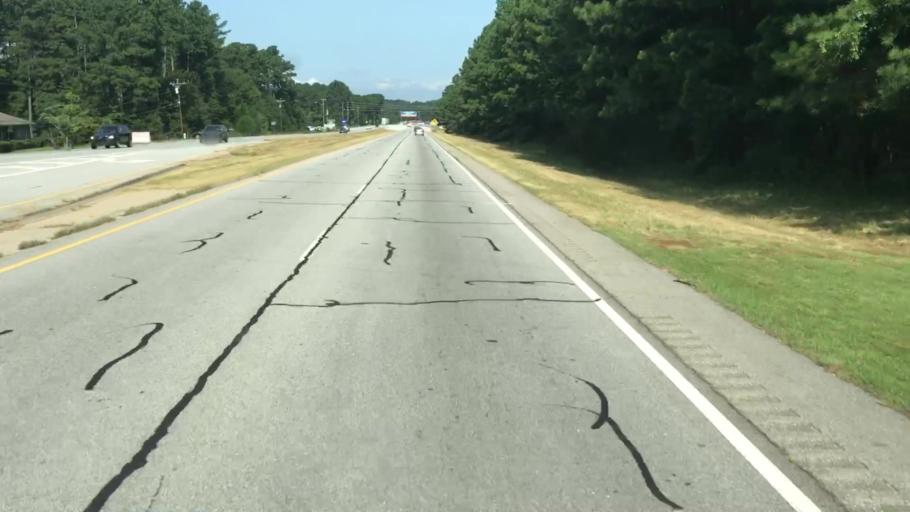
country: US
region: Georgia
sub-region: Walton County
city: Walnut Grove
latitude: 33.8213
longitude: -83.8136
